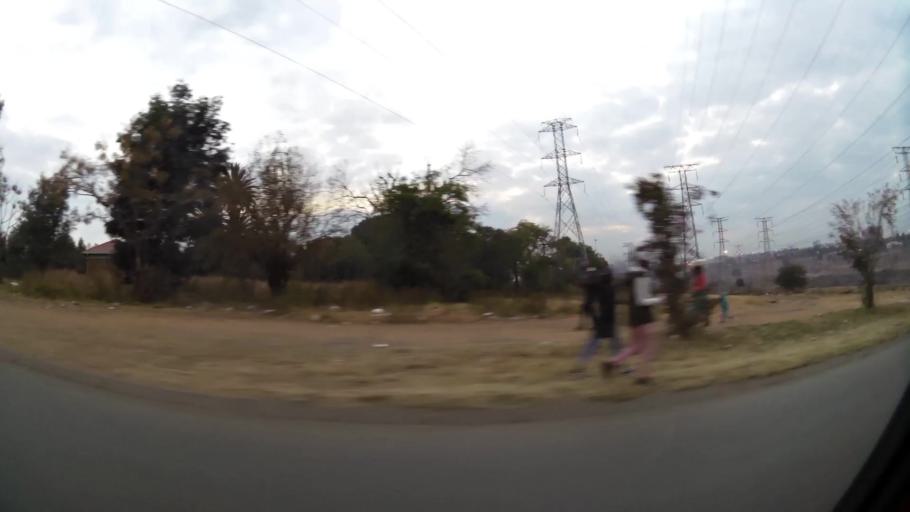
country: ZA
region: Gauteng
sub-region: City of Johannesburg Metropolitan Municipality
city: Soweto
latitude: -26.2526
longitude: 27.9276
